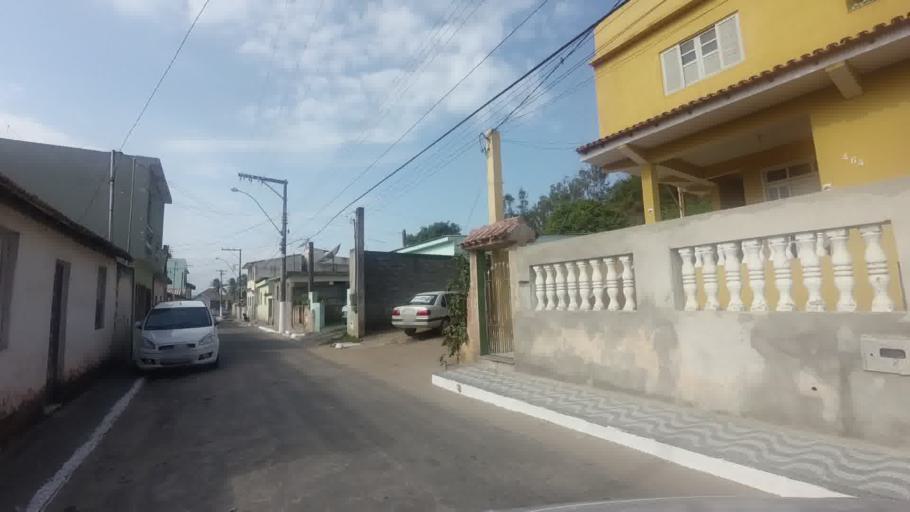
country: BR
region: Espirito Santo
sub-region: Itapemirim
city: Itapemirim
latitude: -21.0065
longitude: -40.8330
